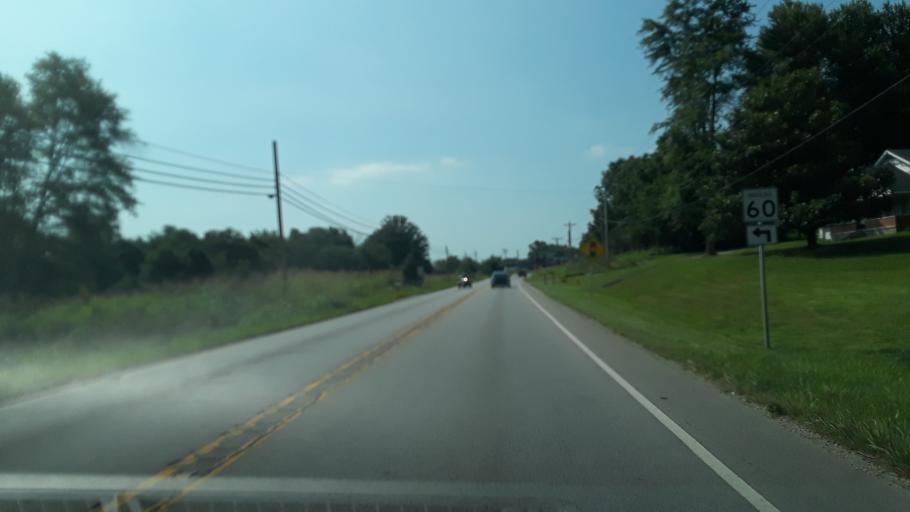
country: US
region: Indiana
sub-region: Clark County
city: Sellersburg
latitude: 38.4284
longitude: -85.8100
